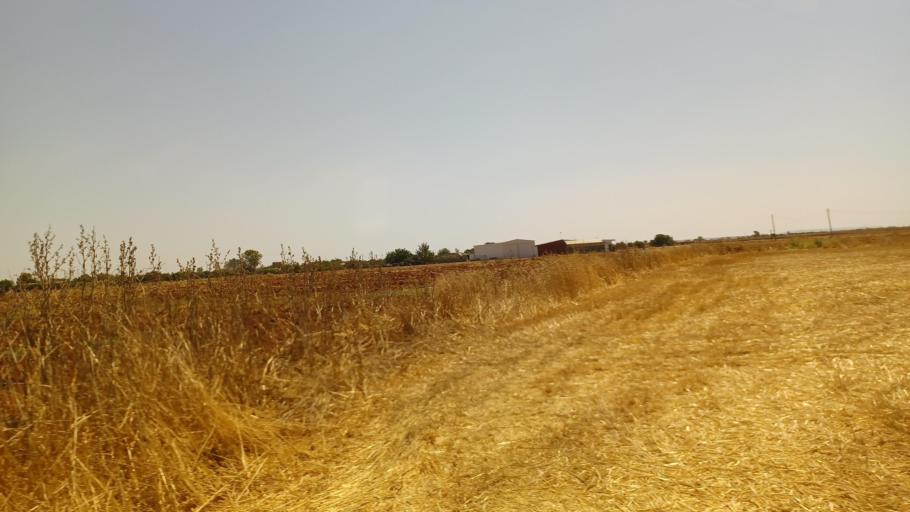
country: CY
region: Ammochostos
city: Avgorou
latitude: 35.0285
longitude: 33.8066
